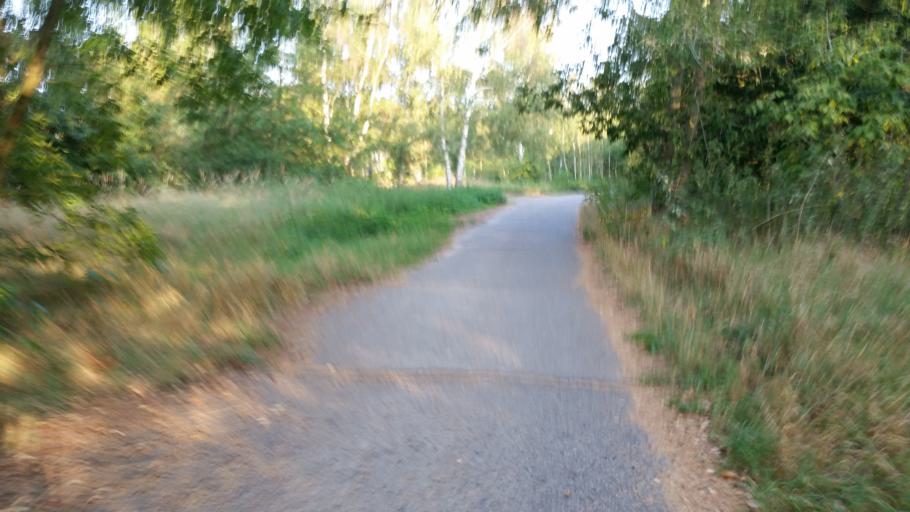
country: DE
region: Berlin
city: Marienfelde
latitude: 52.4083
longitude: 13.3414
